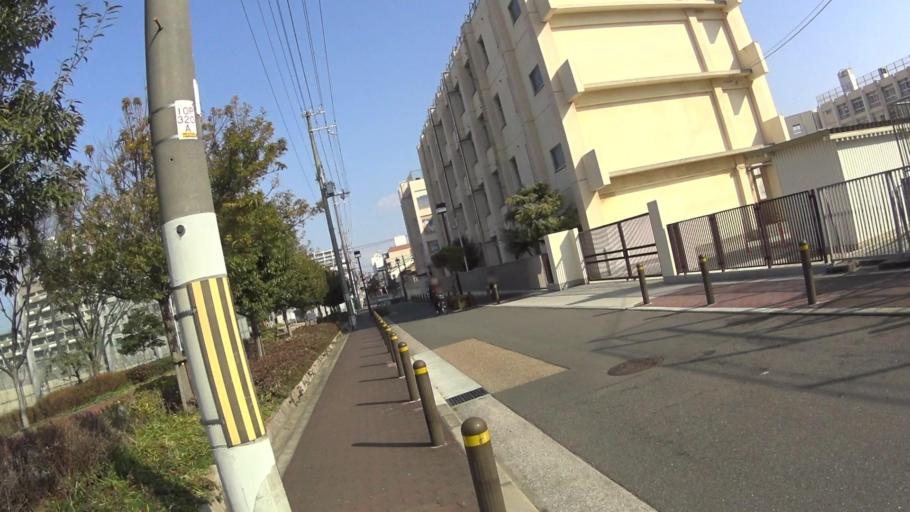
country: JP
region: Osaka
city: Sakai
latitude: 34.6041
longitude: 135.5026
